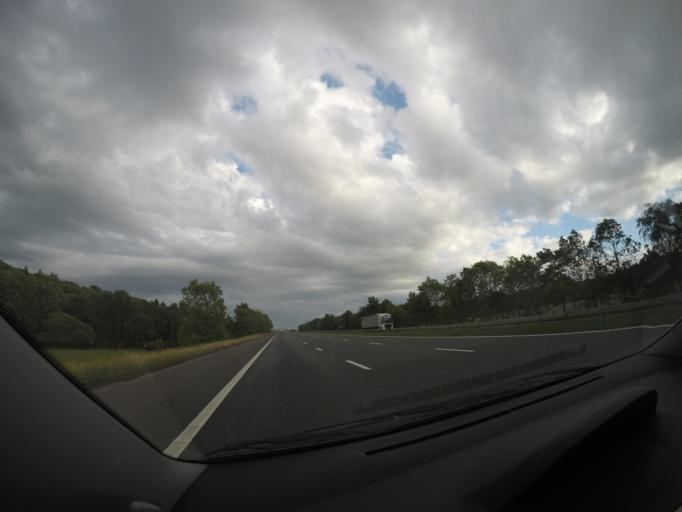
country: GB
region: England
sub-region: Cumbria
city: Penrith
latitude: 54.7445
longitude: -2.8111
